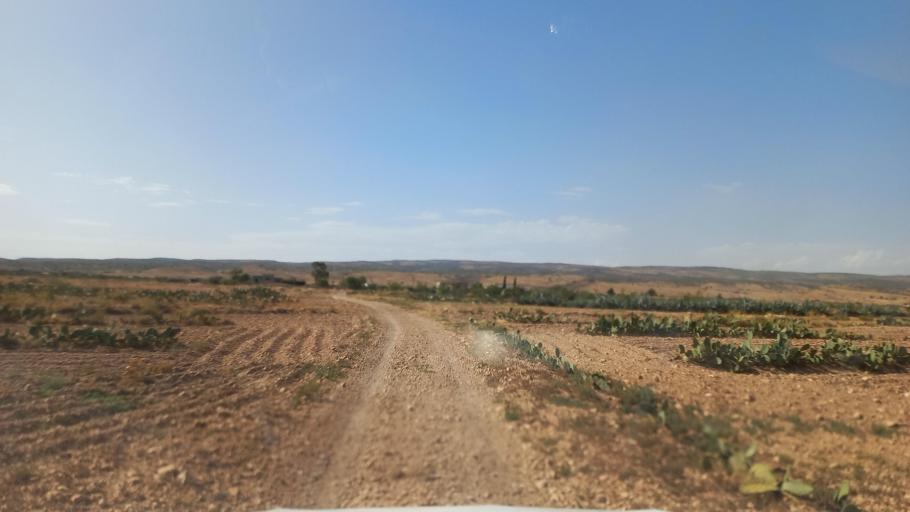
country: TN
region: Al Qasrayn
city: Kasserine
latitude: 35.2856
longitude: 8.9397
